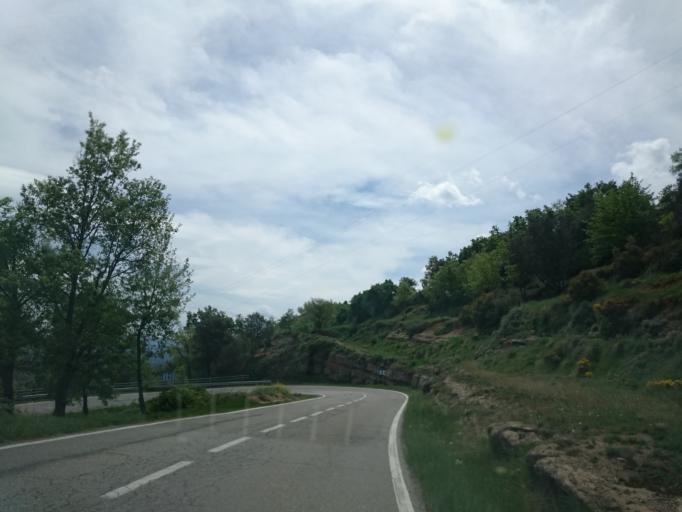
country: ES
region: Catalonia
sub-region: Provincia de Barcelona
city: Prats de Llucanes
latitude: 42.0051
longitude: 2.0420
